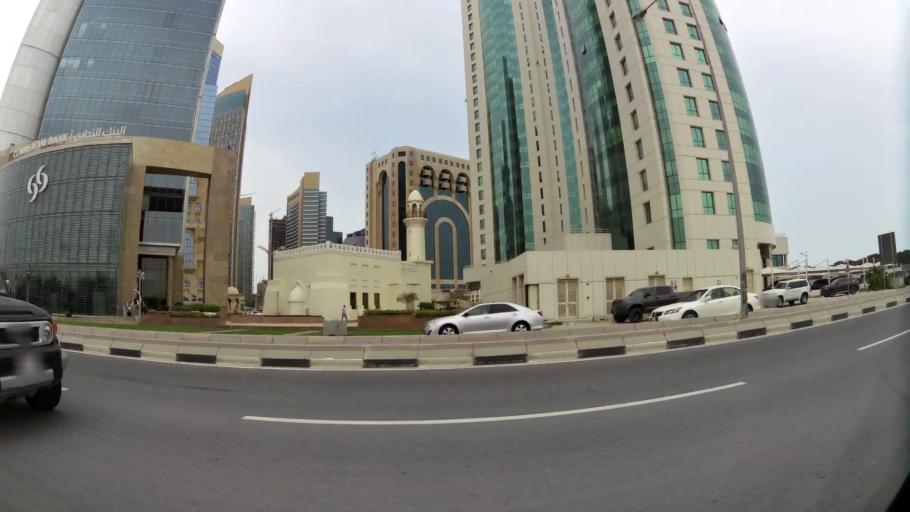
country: QA
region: Baladiyat ad Dawhah
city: Doha
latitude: 25.3126
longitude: 51.5185
